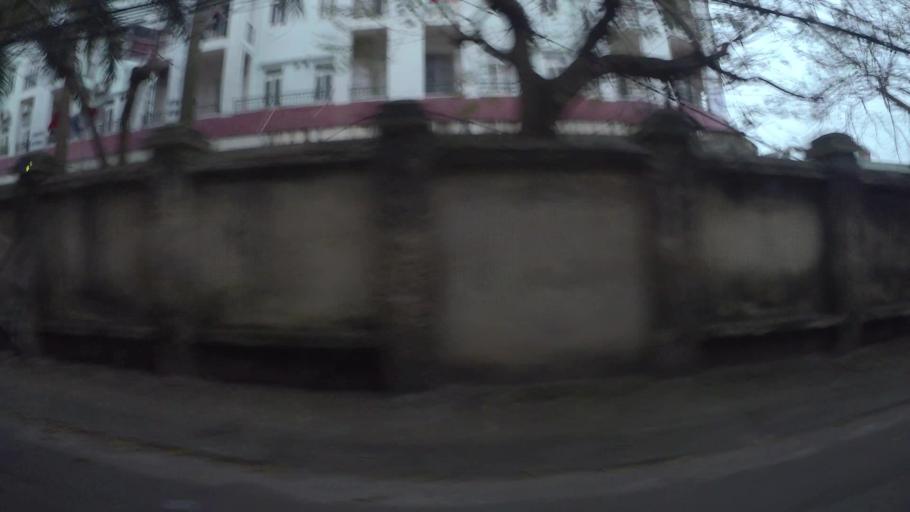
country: VN
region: Ha Noi
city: Trau Quy
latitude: 21.0362
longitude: 105.9041
